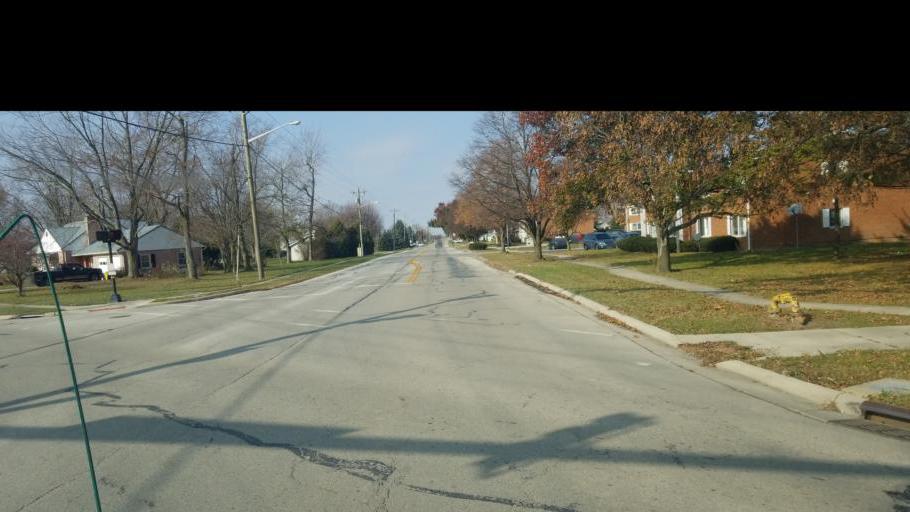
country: US
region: Ohio
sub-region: Mercer County
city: Celina
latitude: 40.5603
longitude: -84.5808
